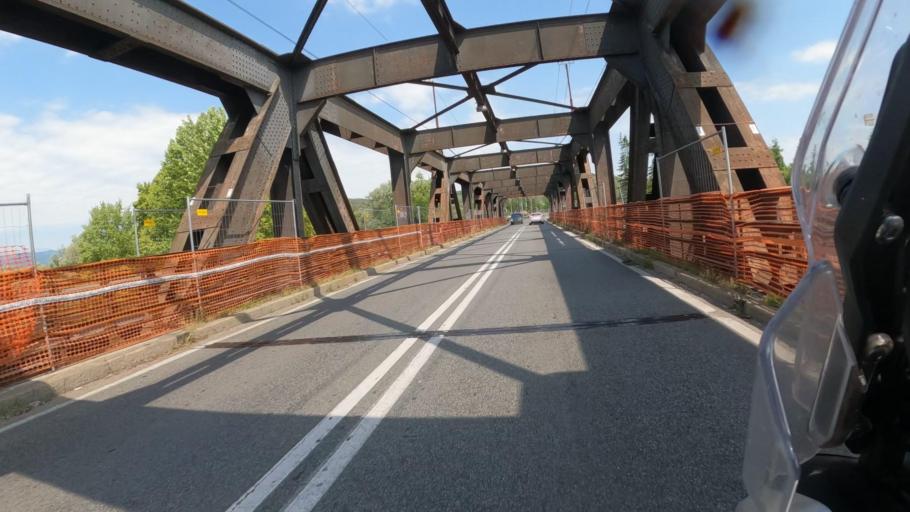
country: IT
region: Piedmont
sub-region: Provincia di Novara
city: Castelletto Sopra Ticino
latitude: 45.7228
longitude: 8.6273
